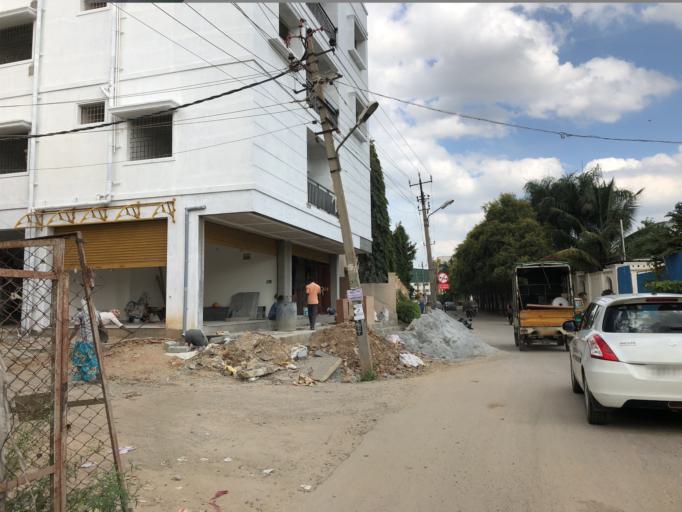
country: IN
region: Karnataka
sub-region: Bangalore Urban
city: Bangalore
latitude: 12.9906
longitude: 77.6932
